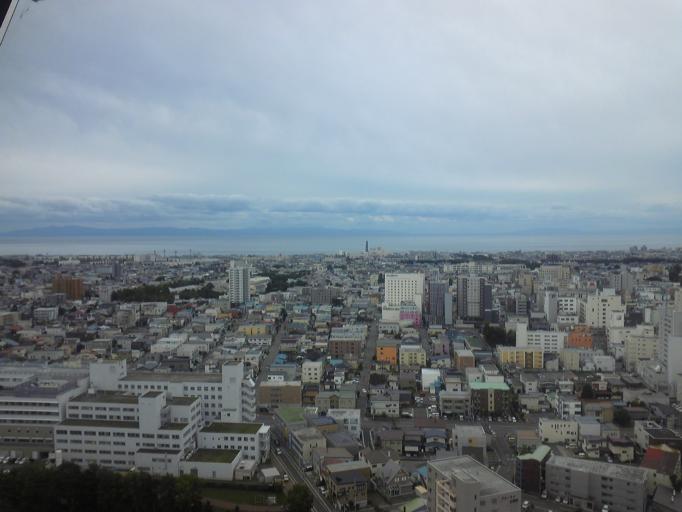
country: JP
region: Hokkaido
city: Hakodate
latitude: 41.7947
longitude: 140.7536
